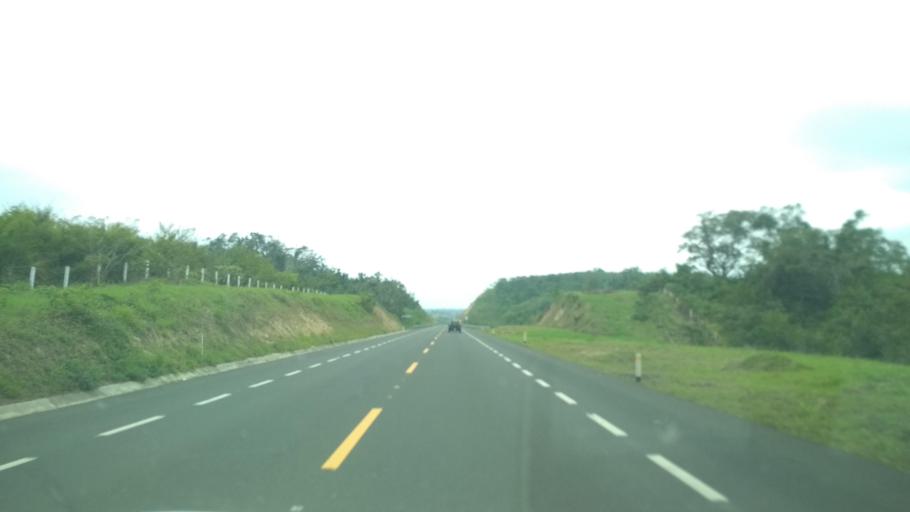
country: MX
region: Veracruz
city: Agua Dulce
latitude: 20.4196
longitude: -97.2145
